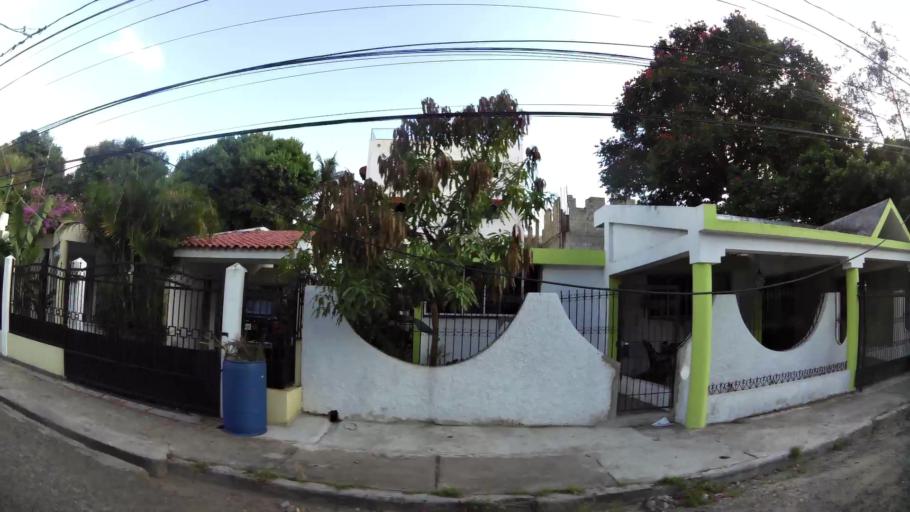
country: DO
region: Santiago
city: Santiago de los Caballeros
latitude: 19.4602
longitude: -70.6943
